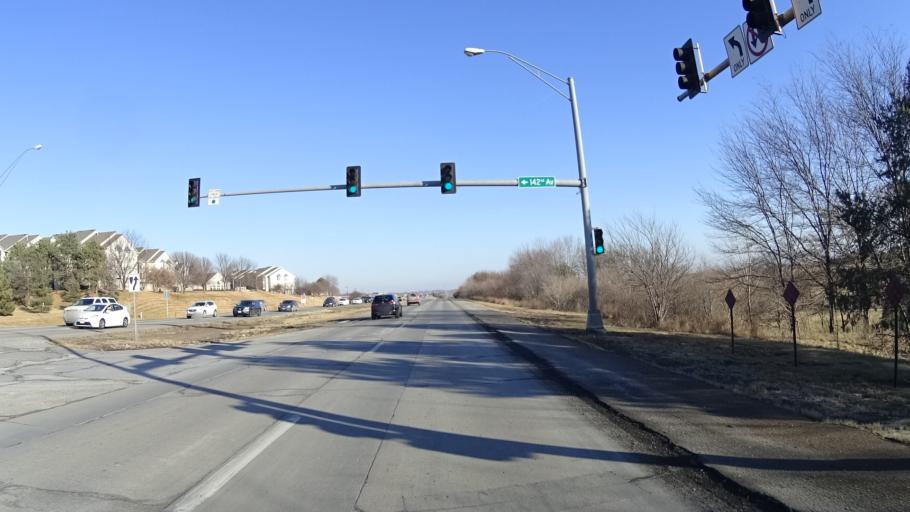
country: US
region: Nebraska
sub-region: Douglas County
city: Bennington
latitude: 41.2920
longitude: -96.1337
